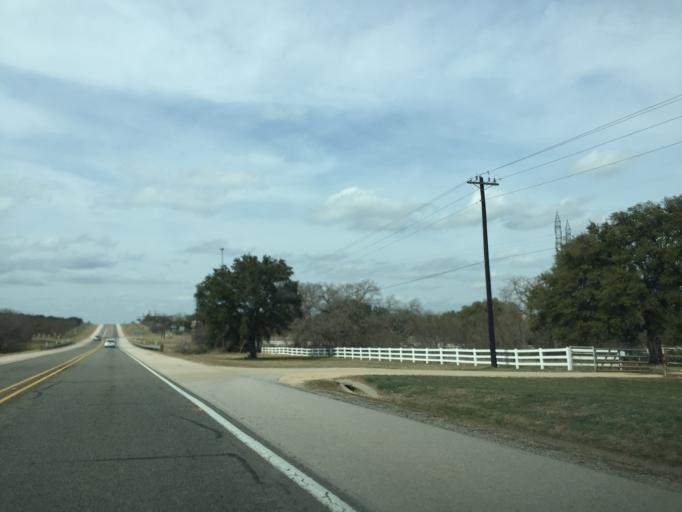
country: US
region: Texas
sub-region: Burnet County
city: Granite Shoals
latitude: 30.5261
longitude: -98.4203
